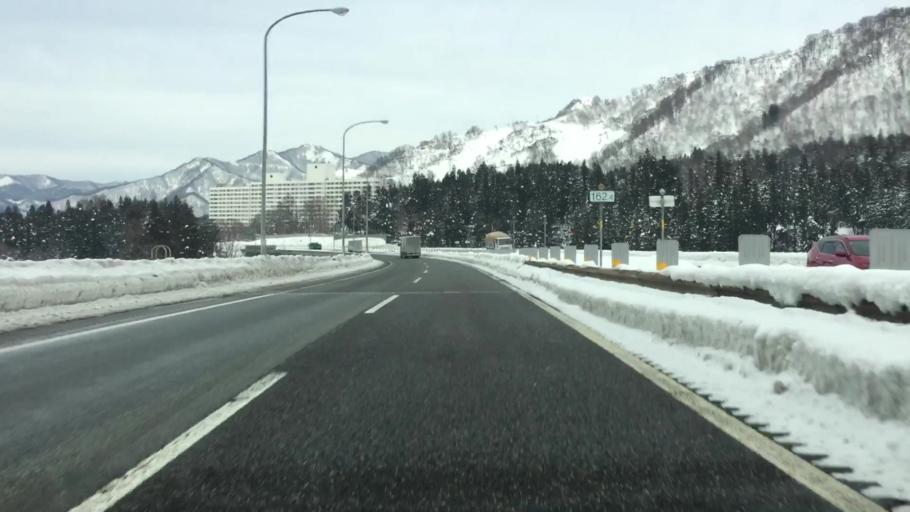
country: JP
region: Niigata
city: Shiozawa
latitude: 36.8993
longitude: 138.8465
